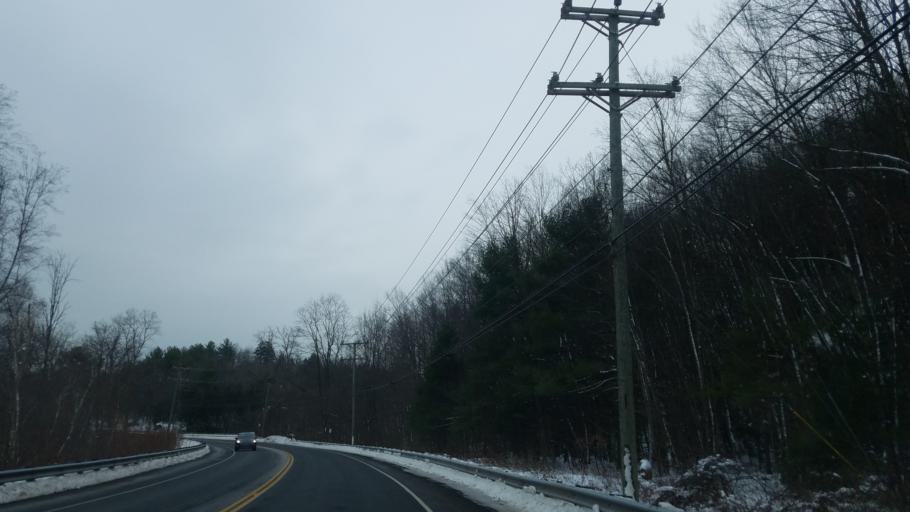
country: US
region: Connecticut
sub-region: Litchfield County
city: New Hartford Center
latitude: 41.8563
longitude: -72.9589
